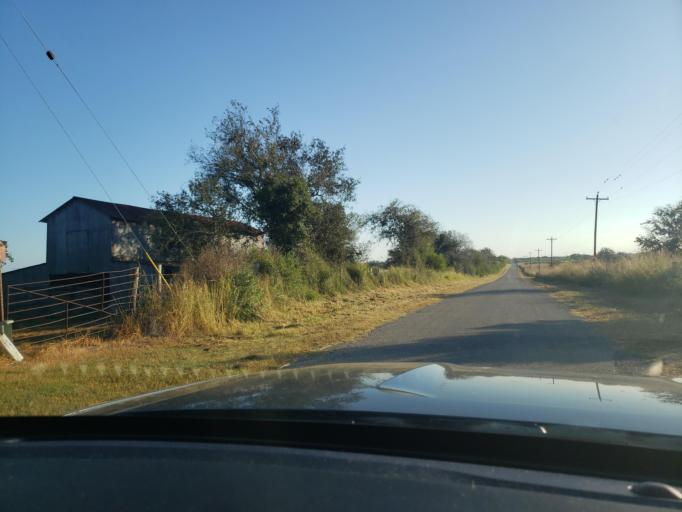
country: US
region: Texas
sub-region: Bee County
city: Beeville
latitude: 28.4174
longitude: -97.7189
